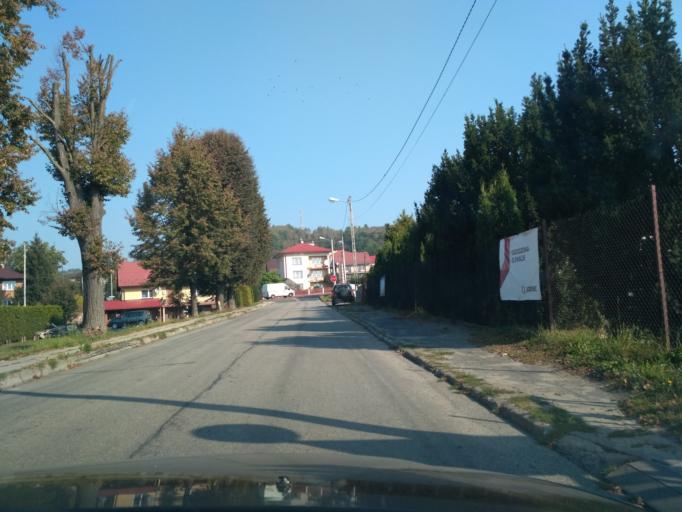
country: PL
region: Subcarpathian Voivodeship
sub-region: Powiat strzyzowski
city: Strzyzow
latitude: 49.8717
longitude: 21.8009
